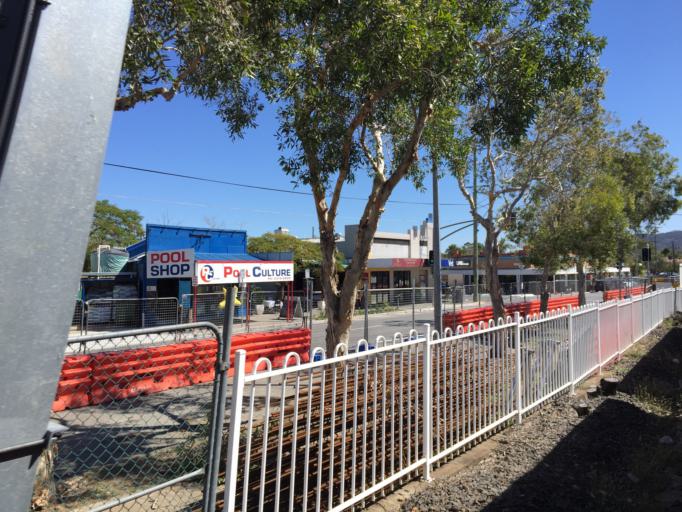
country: AU
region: Queensland
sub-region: Brisbane
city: Taringa
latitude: -27.5215
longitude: 152.9763
